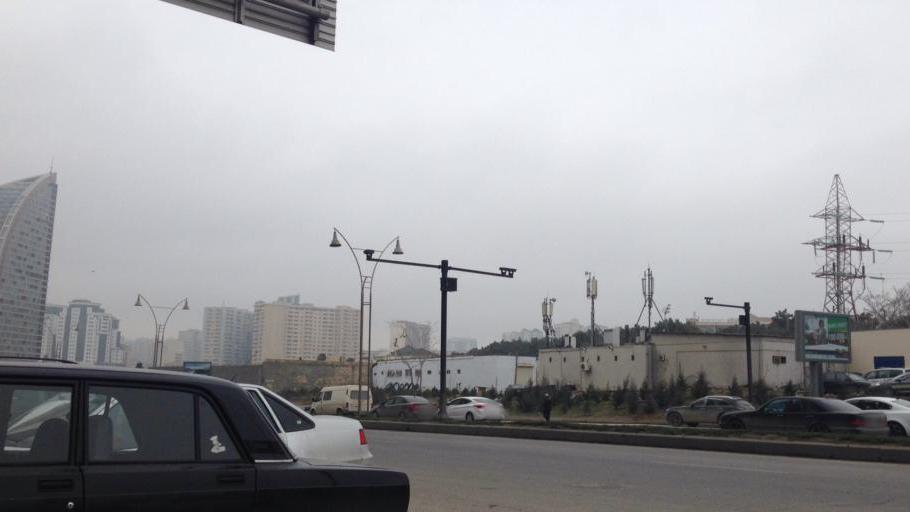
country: AZ
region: Baki
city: Baku
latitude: 40.3896
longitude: 49.8722
